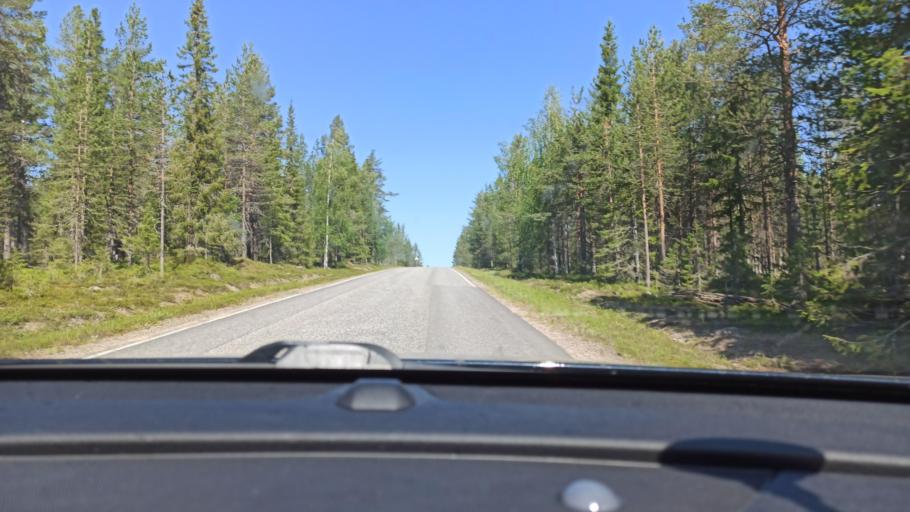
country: FI
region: Lapland
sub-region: Tunturi-Lappi
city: Kolari
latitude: 67.6791
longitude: 24.1401
